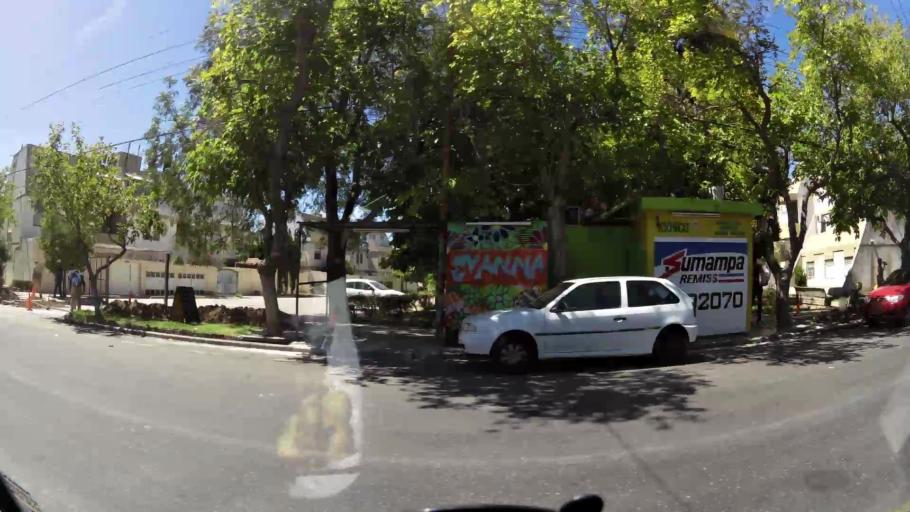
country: AR
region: San Juan
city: San Juan
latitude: -31.5270
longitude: -68.5224
